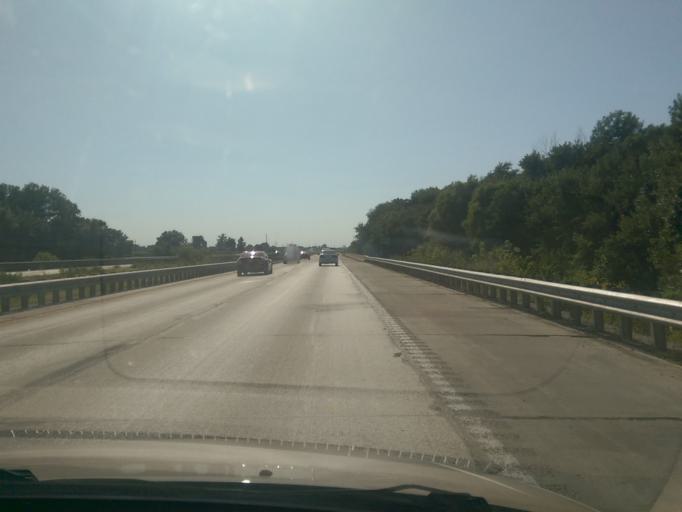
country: US
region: Missouri
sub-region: Saline County
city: Sweet Springs
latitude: 38.9778
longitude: -93.4356
